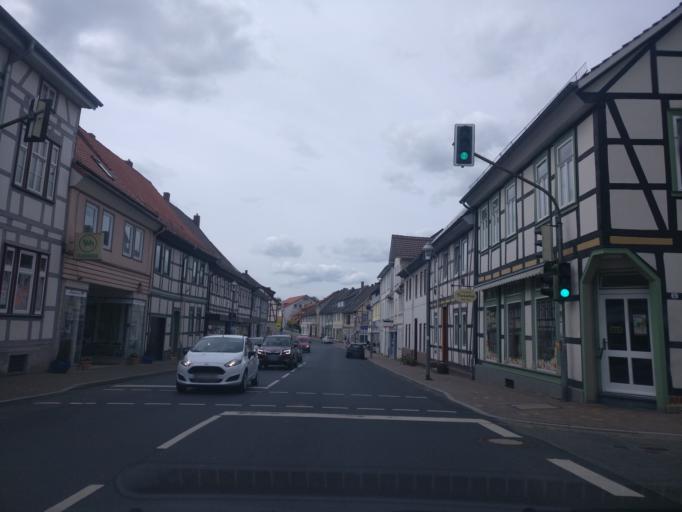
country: DE
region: Lower Saxony
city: Dransfeld
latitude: 51.5029
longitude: 9.7594
